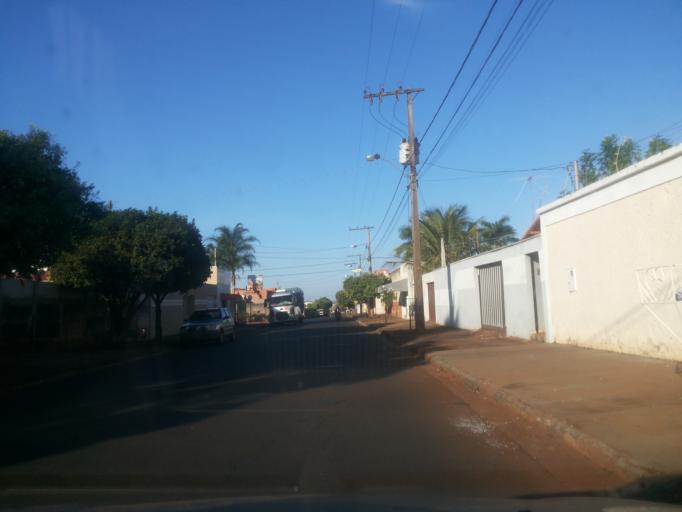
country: BR
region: Minas Gerais
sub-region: Ituiutaba
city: Ituiutaba
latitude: -18.9943
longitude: -49.4532
